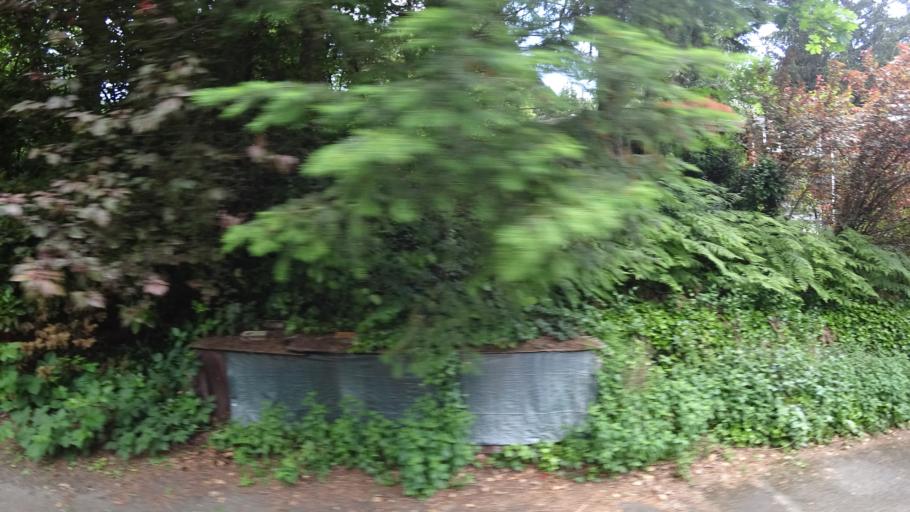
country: US
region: Oregon
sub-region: Washington County
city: Garden Home-Whitford
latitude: 45.4588
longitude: -122.7225
